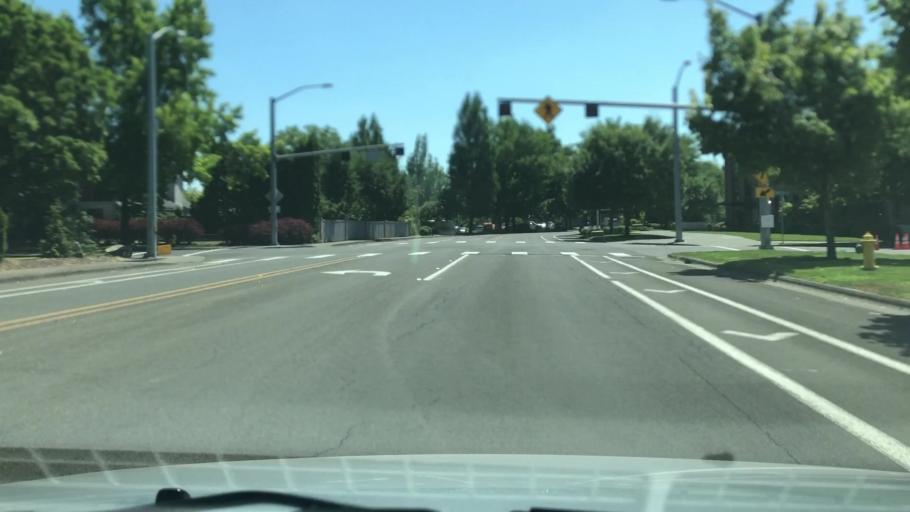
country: US
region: Oregon
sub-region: Clackamas County
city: Wilsonville
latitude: 45.3054
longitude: -122.7595
